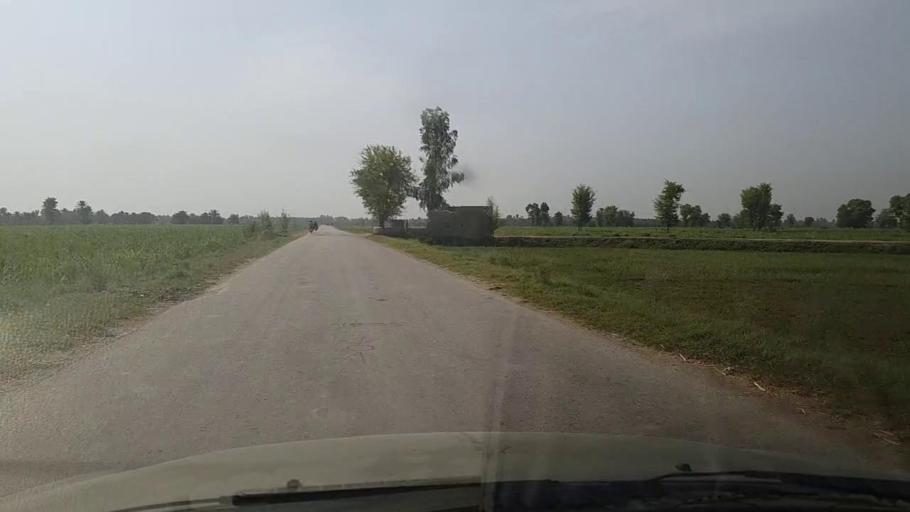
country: PK
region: Sindh
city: Gambat
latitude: 27.4644
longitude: 68.4795
